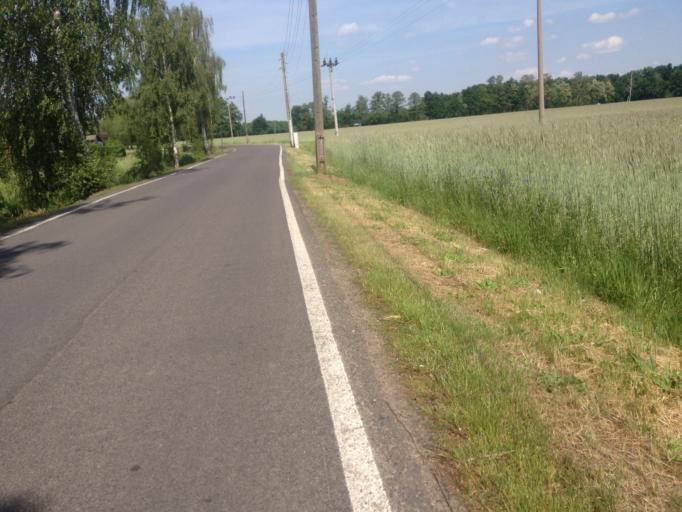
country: DE
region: Brandenburg
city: Cottbus
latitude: 51.8172
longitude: 14.3252
